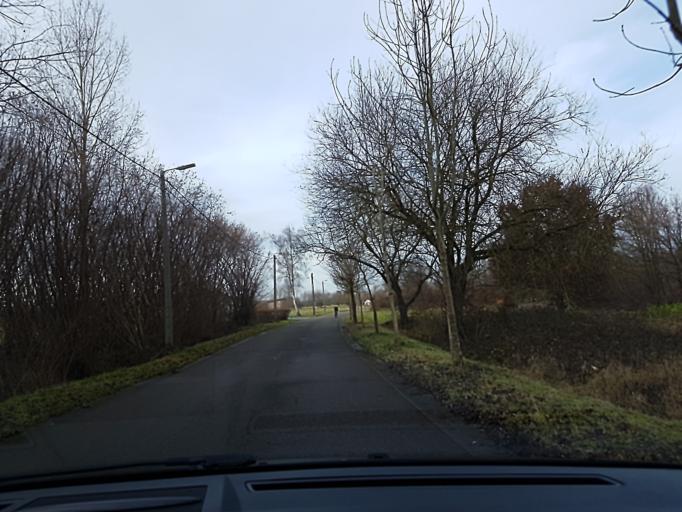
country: BE
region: Flanders
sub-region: Provincie Vlaams-Brabant
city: Rotselaar
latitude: 50.9403
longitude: 4.7102
